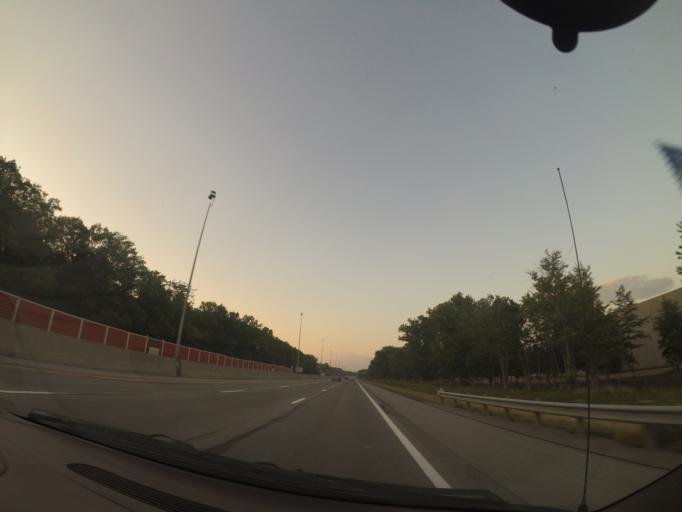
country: US
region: Ohio
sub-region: Lake County
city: Mentor
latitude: 41.7011
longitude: -81.3176
